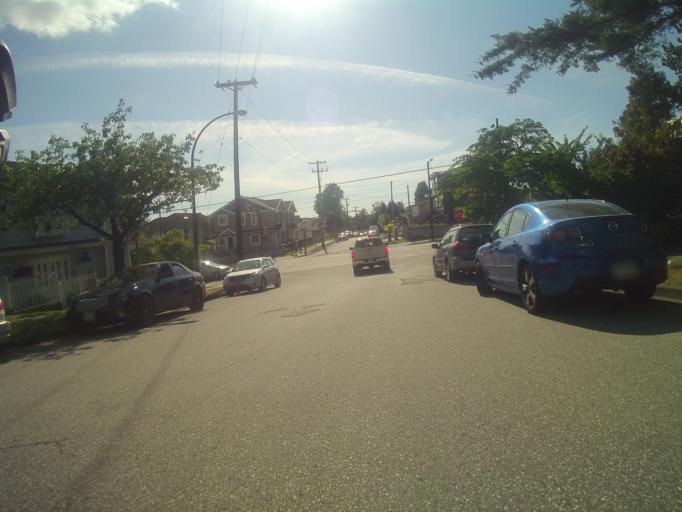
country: CA
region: British Columbia
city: Vancouver
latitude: 49.2166
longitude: -123.0905
